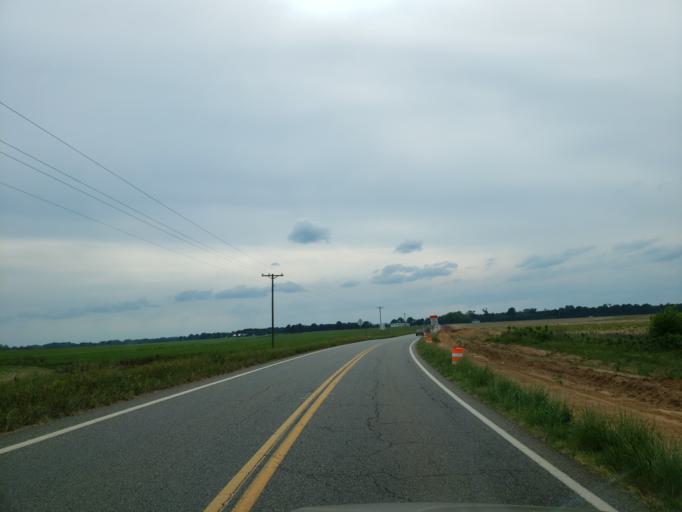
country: US
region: Georgia
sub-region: Macon County
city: Marshallville
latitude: 32.3581
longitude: -83.9300
